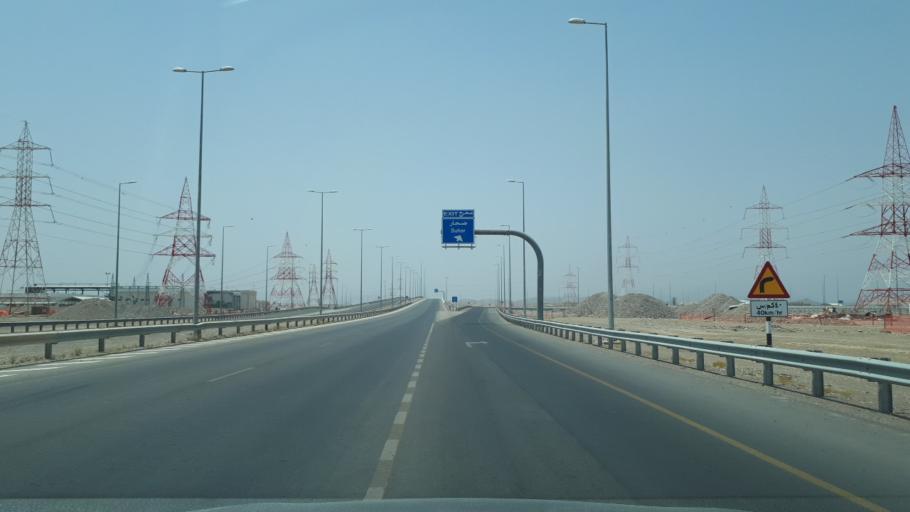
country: OM
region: Muhafazat Masqat
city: As Sib al Jadidah
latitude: 23.6133
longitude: 58.0917
